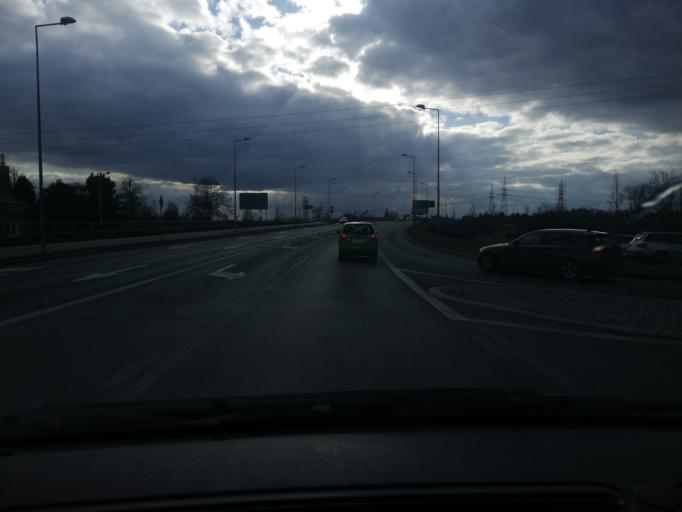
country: PL
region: Silesian Voivodeship
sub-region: Czestochowa
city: Czestochowa
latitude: 50.8321
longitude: 19.1489
